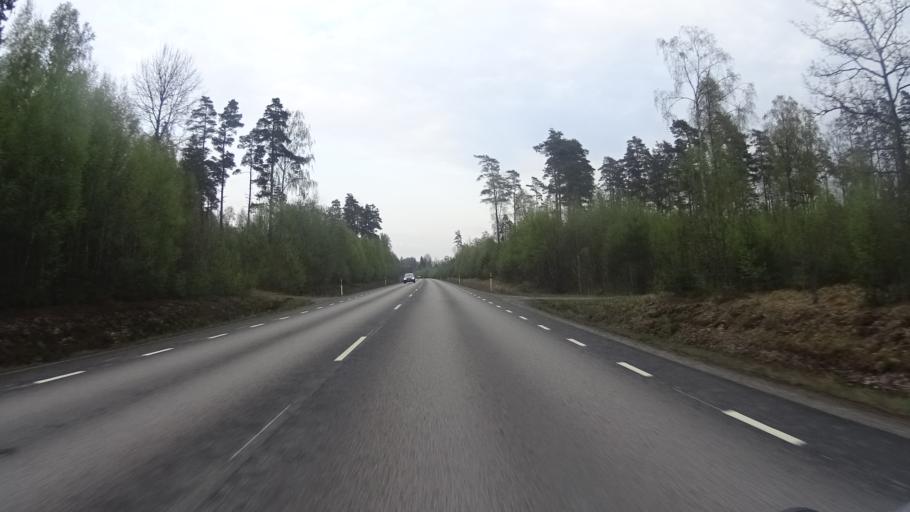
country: SE
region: Kronoberg
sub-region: Ljungby Kommun
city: Ljungby
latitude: 56.8240
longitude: 13.9610
